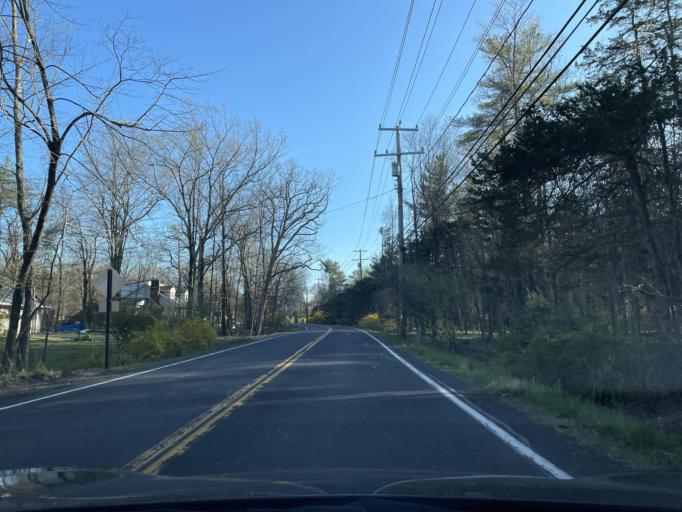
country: US
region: New York
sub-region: Ulster County
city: Woodstock
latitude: 42.0214
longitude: -74.1102
